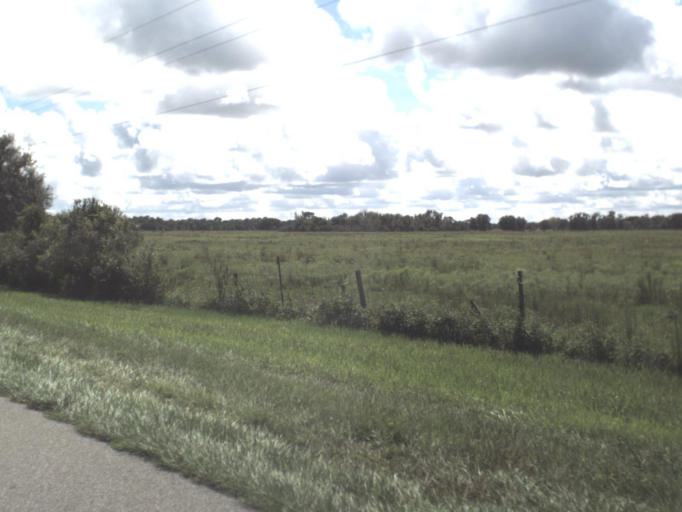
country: US
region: Florida
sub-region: Sarasota County
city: Lake Sarasota
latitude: 27.3662
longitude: -82.2084
